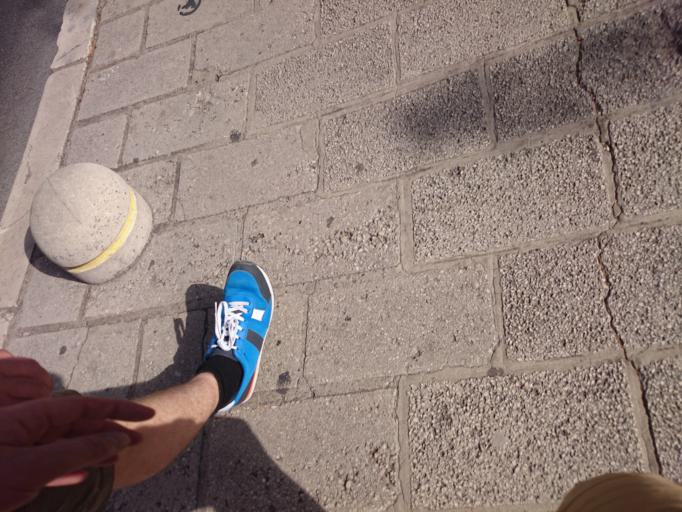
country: HR
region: Dubrovacko-Neretvanska
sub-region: Grad Dubrovnik
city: Dubrovnik
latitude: 42.6447
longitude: 18.0994
